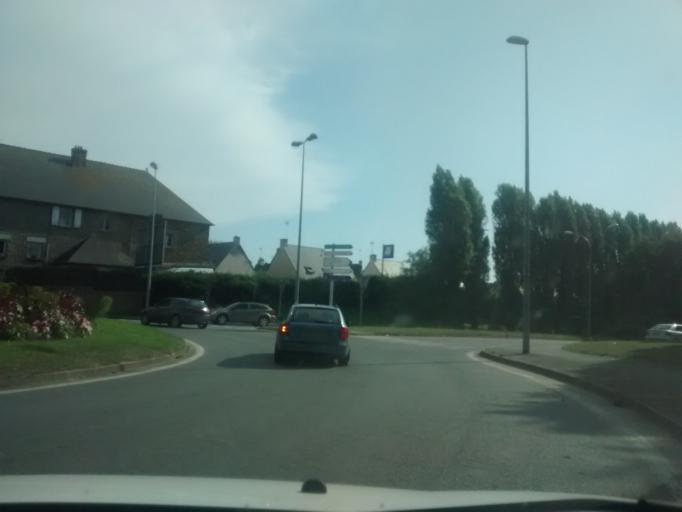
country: FR
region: Brittany
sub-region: Departement d'Ille-et-Vilaine
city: Saint-Malo
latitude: 48.6480
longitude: -1.9842
